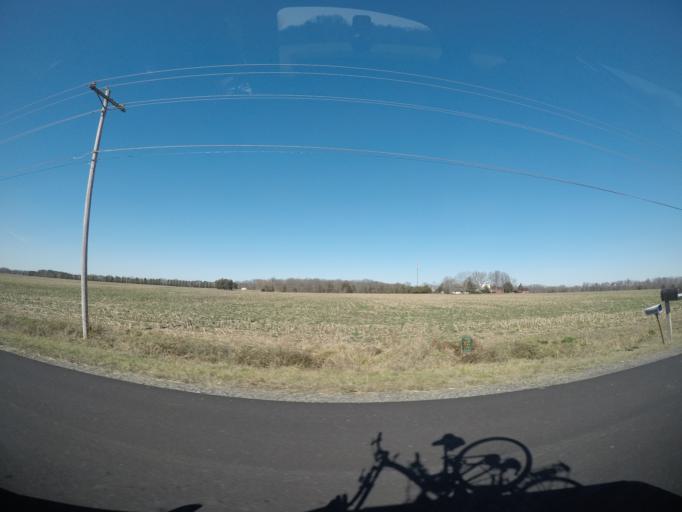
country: US
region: Delaware
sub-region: New Castle County
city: Townsend
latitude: 39.3600
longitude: -75.8289
